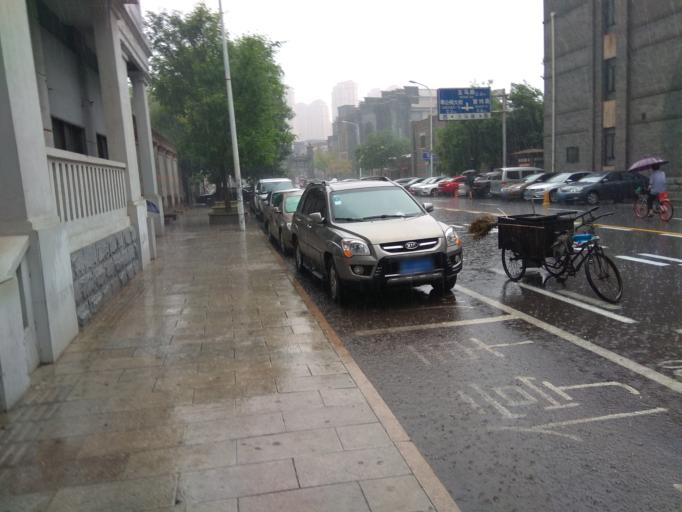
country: CN
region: Tianjin Shi
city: Hongshunli
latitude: 39.1522
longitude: 117.1867
